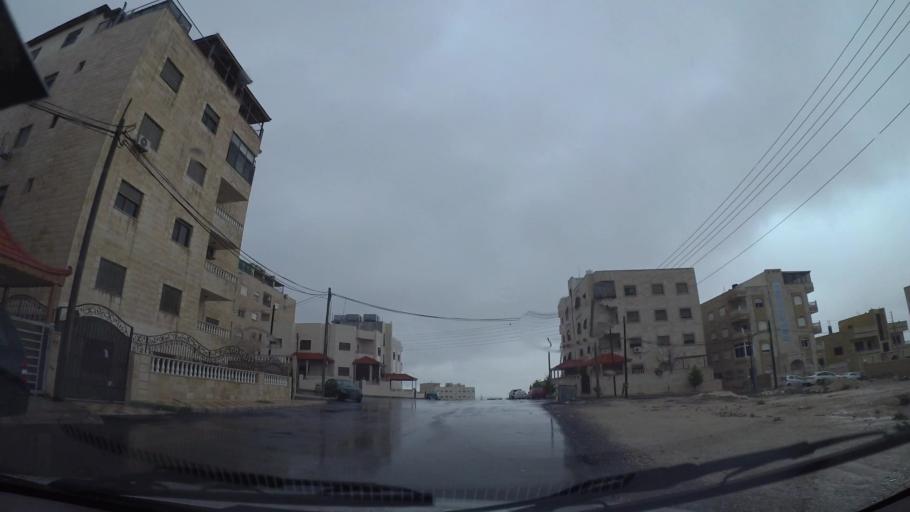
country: JO
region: Amman
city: Al Jubayhah
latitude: 32.0448
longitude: 35.8937
